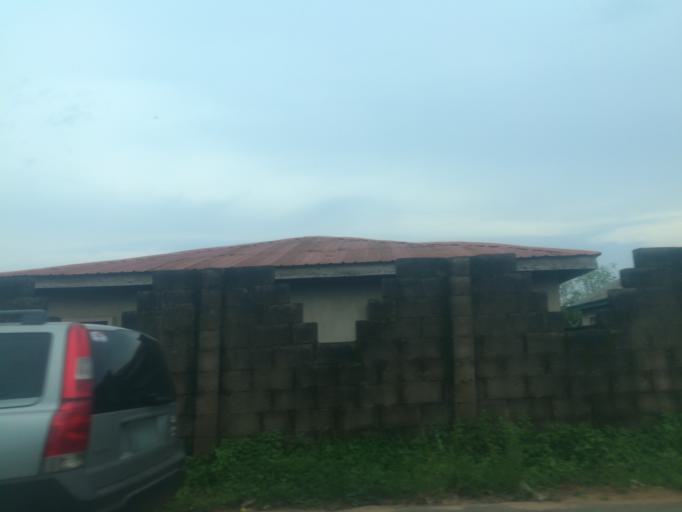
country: NG
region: Oyo
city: Ibadan
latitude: 7.3685
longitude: 3.8221
